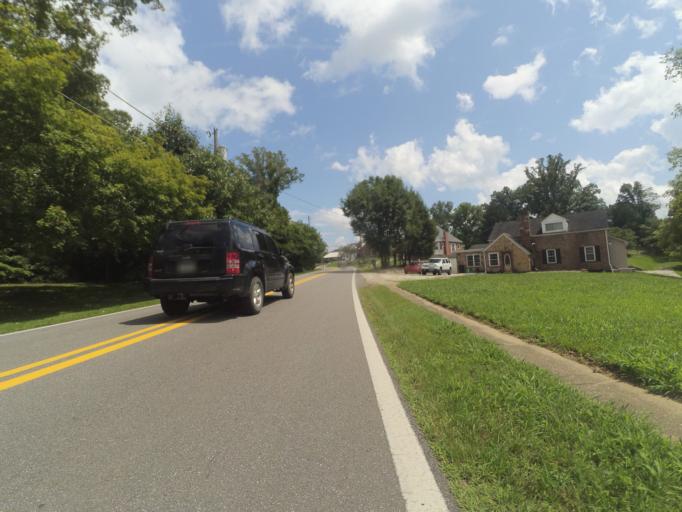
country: US
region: West Virginia
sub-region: Cabell County
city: Pea Ridge
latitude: 38.4099
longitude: -82.3460
